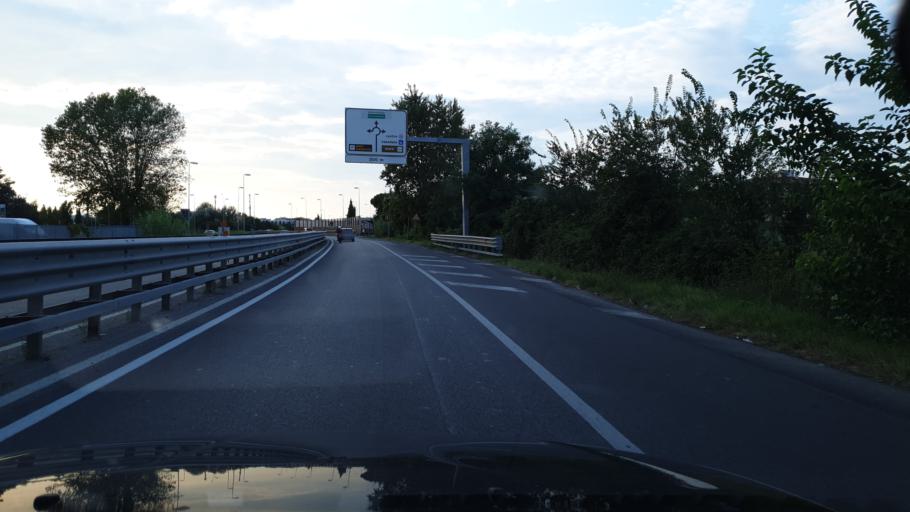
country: IT
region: Emilia-Romagna
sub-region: Provincia di Rimini
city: Rivazzurra
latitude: 44.0395
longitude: 12.5942
